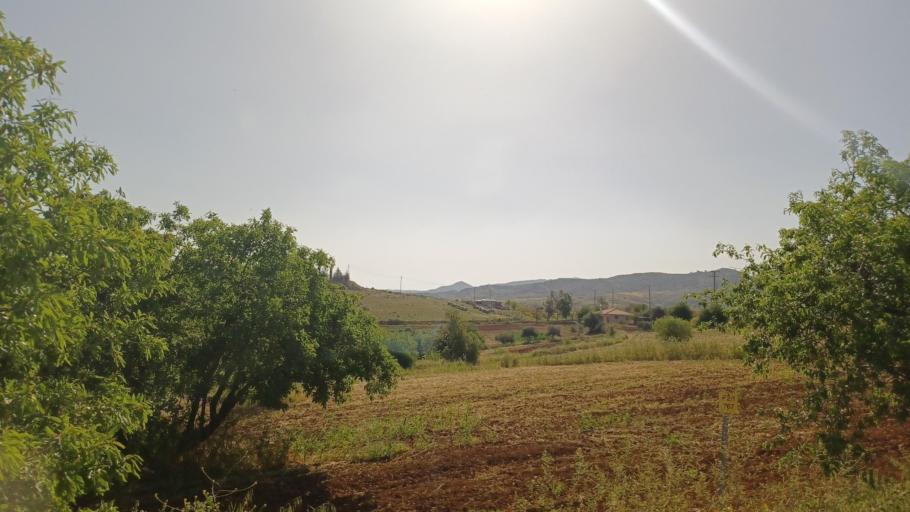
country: CY
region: Lefkosia
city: Astromeritis
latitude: 35.0790
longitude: 33.0181
